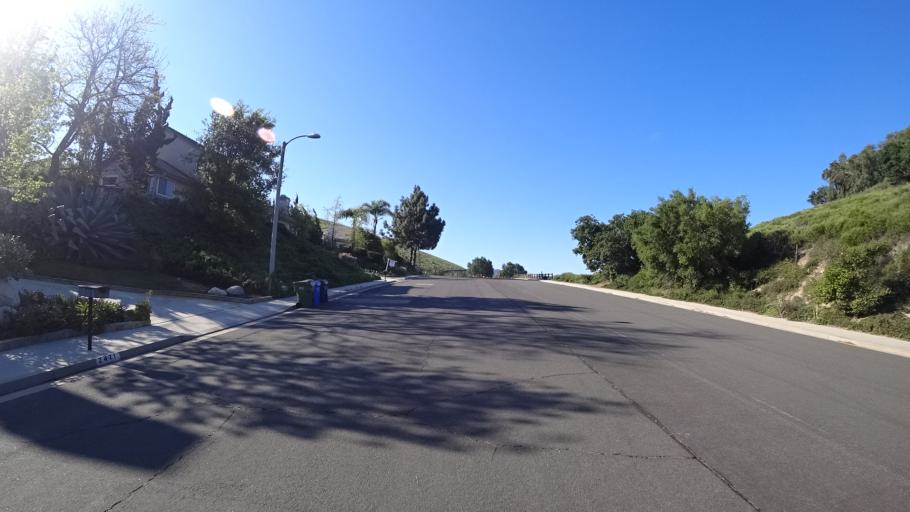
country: US
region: California
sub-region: Ventura County
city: Thousand Oaks
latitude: 34.1867
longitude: -118.8375
